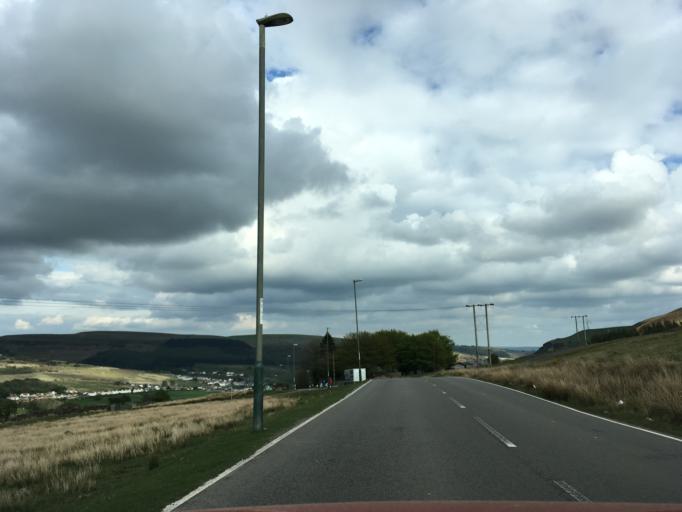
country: GB
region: Wales
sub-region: Caerphilly County Borough
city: Rhymney
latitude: 51.7457
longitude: -3.2906
